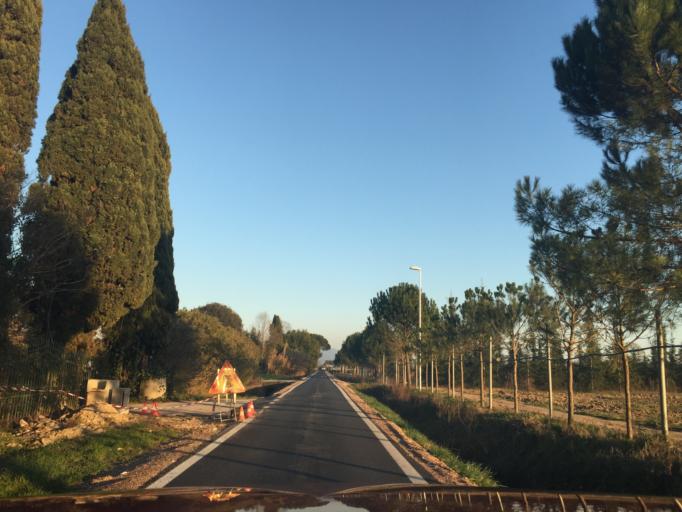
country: IT
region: Tuscany
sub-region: Provincia di Pistoia
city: Ponte Buggianese
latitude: 43.8584
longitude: 10.7643
